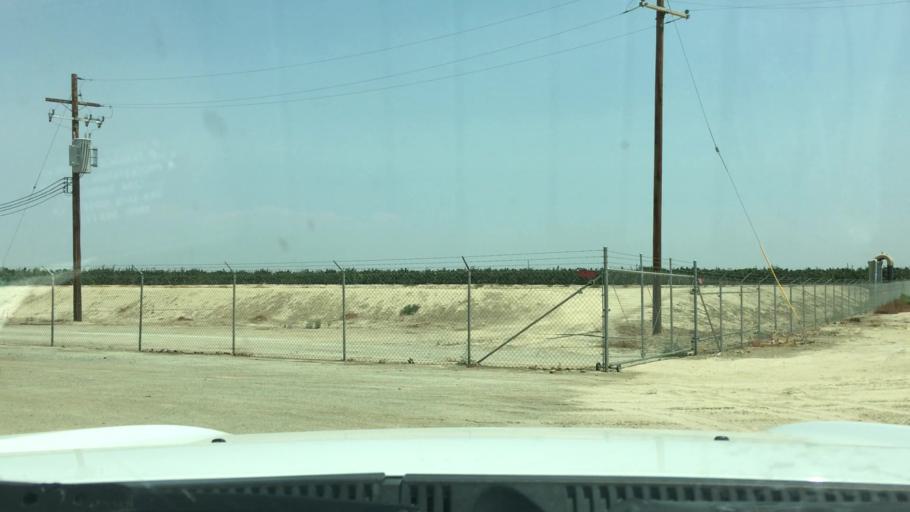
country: US
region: California
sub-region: Kern County
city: Wasco
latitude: 35.6815
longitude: -119.4199
